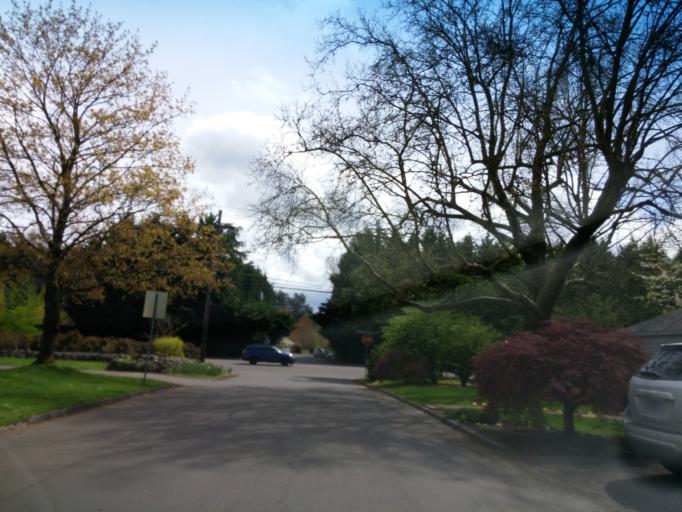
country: US
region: Oregon
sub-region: Washington County
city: Cedar Hills
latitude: 45.5053
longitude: -122.7989
